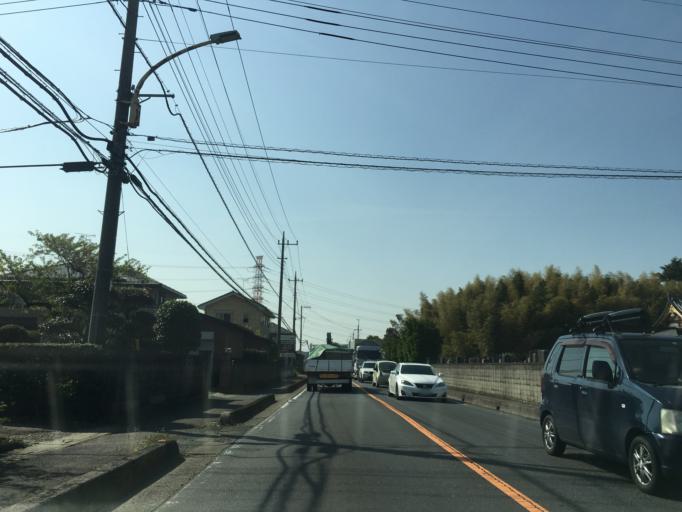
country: JP
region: Saitama
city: Sugito
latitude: 36.0053
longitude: 139.7014
